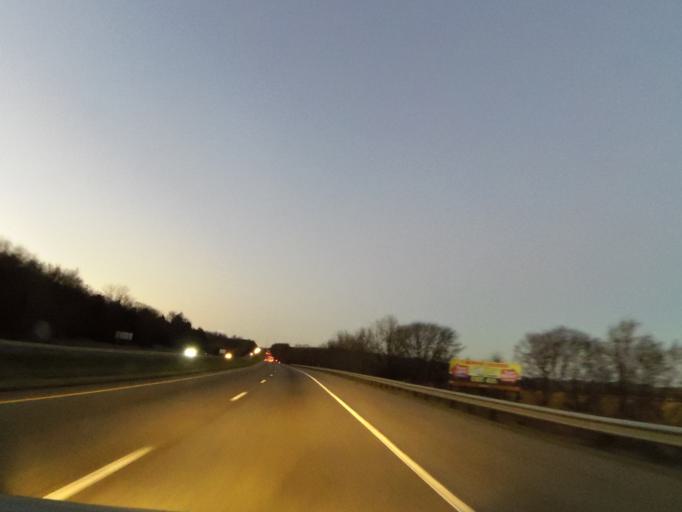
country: US
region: Tennessee
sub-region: Cocke County
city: Newport
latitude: 35.9027
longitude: -83.1838
